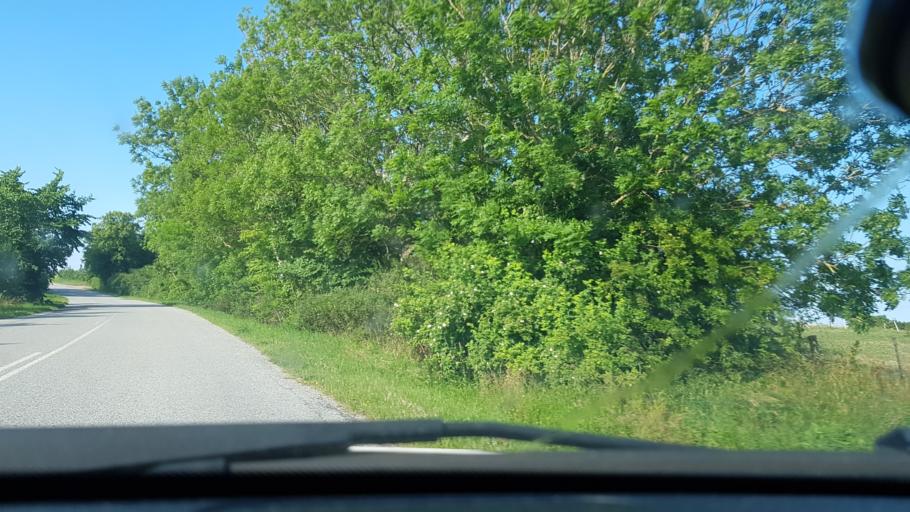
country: DK
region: Zealand
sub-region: Odsherred Kommune
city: Hojby
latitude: 55.8923
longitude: 11.6149
